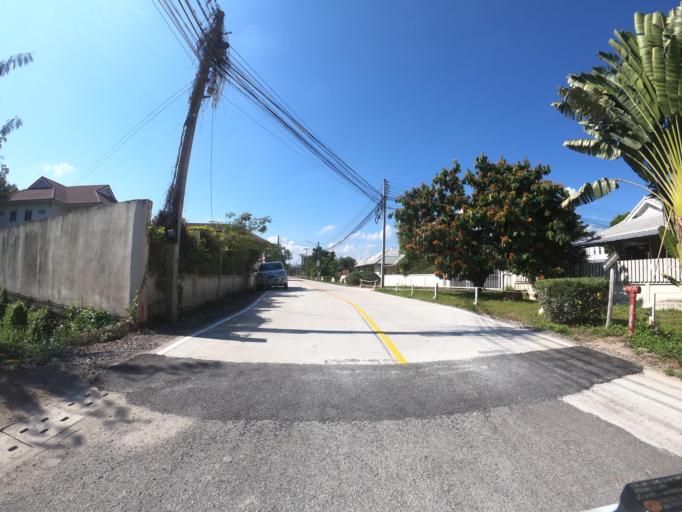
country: TH
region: Chiang Mai
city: Chiang Mai
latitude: 18.7439
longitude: 98.9678
